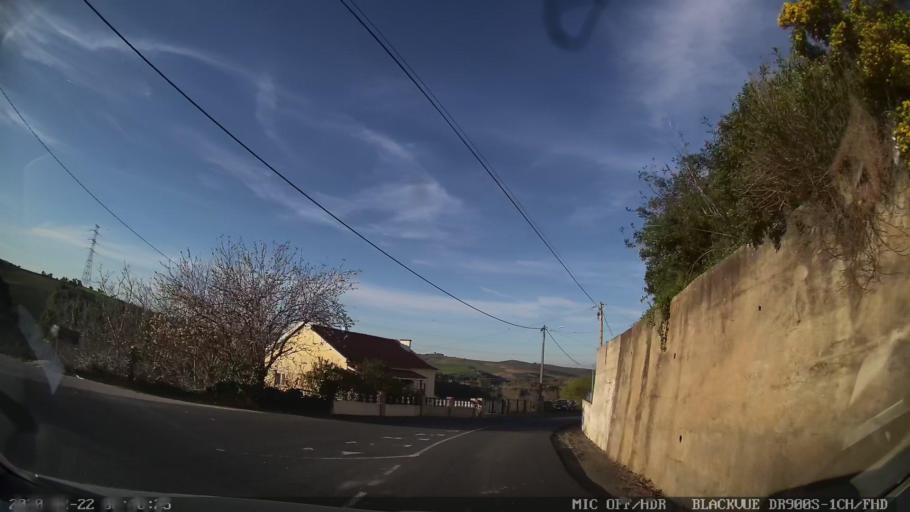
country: PT
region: Lisbon
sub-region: Vila Franca de Xira
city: Castanheira do Ribatejo
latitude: 38.9905
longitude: -9.0172
